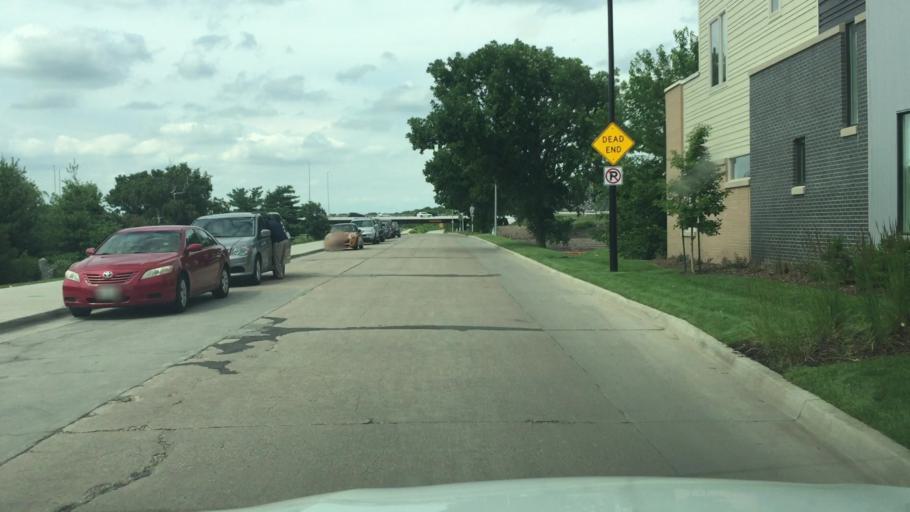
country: US
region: Iowa
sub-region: Polk County
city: Des Moines
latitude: 41.5931
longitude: -93.6171
